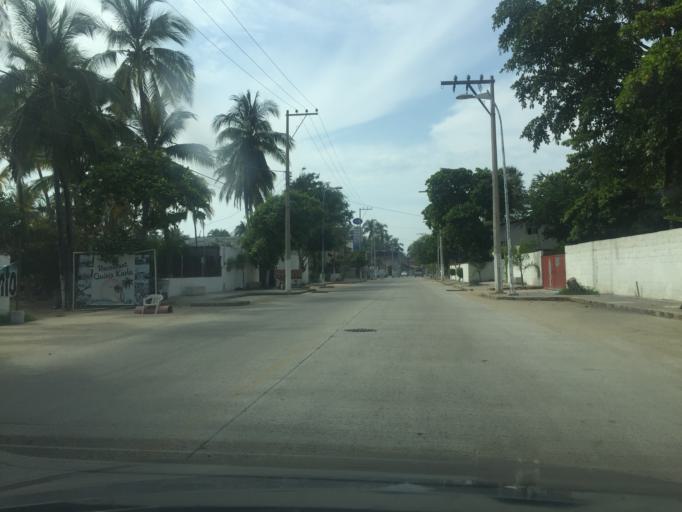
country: MX
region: Guerrero
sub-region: Coyuca de Benitez
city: Colonia Luces en el Mar
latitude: 16.8983
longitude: -99.9646
